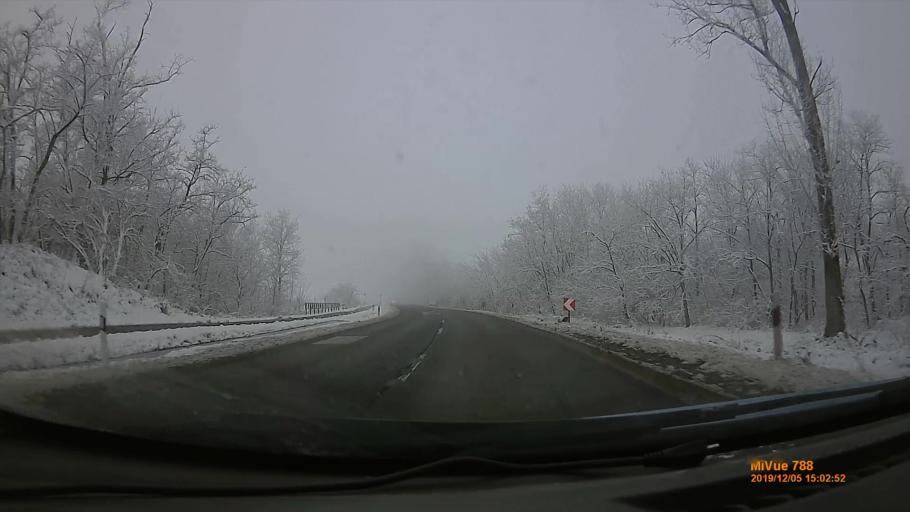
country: HU
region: Szabolcs-Szatmar-Bereg
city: Tiszanagyfalu
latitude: 48.0800
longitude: 21.5075
